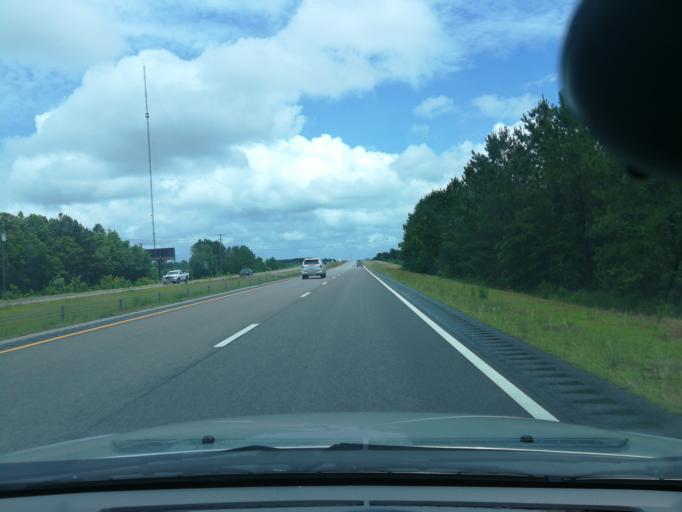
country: US
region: North Carolina
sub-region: Tyrrell County
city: Columbia
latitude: 35.8902
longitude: -76.3548
